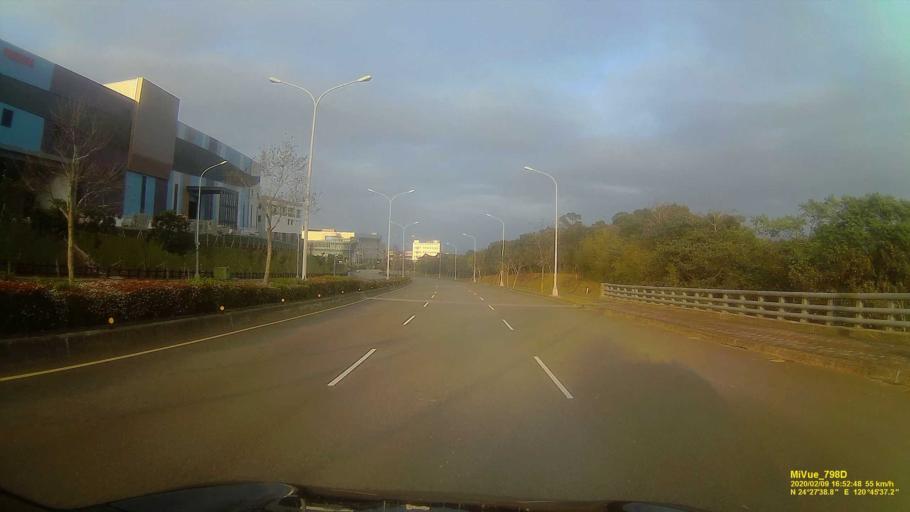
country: TW
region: Taiwan
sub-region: Miaoli
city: Miaoli
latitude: 24.4610
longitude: 120.7606
